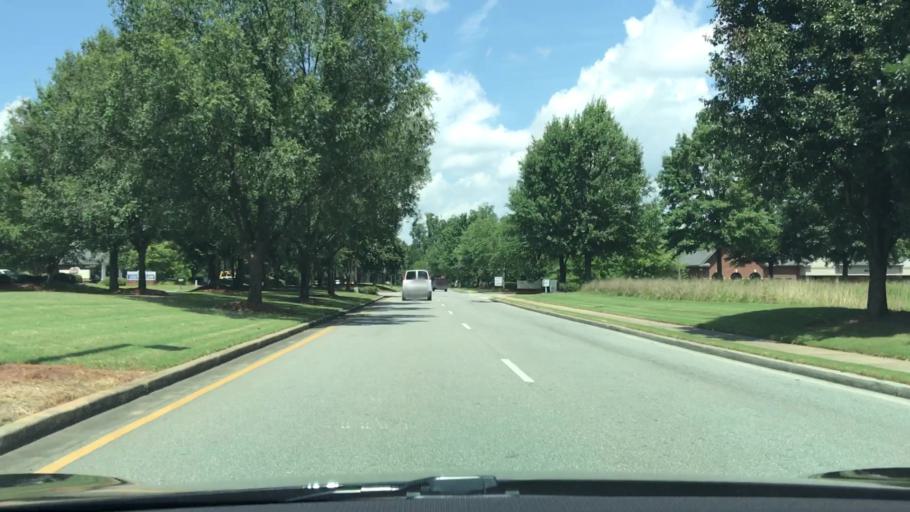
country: US
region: Georgia
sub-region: Fulton County
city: Johns Creek
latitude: 34.0691
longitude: -84.1623
